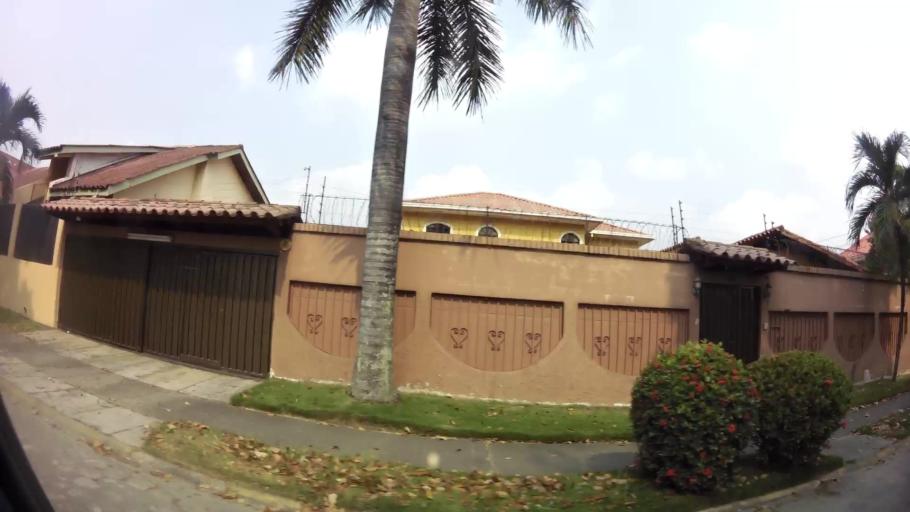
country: HN
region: Cortes
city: San Pedro Sula
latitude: 15.5248
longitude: -88.0276
